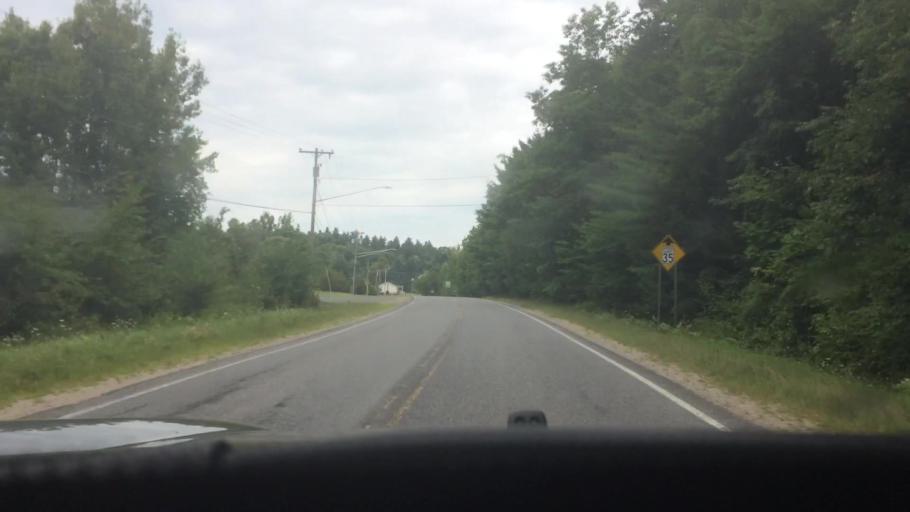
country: US
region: New York
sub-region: St. Lawrence County
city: Hannawa Falls
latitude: 44.5501
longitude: -74.9301
